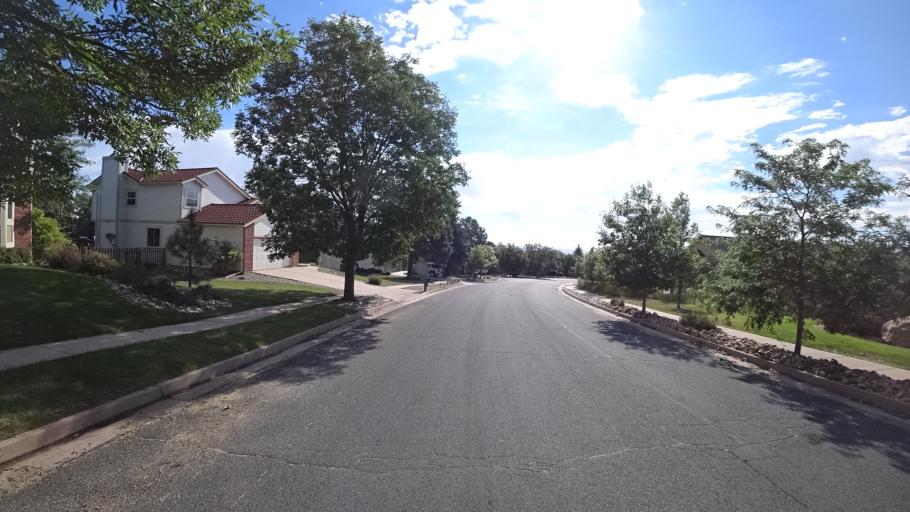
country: US
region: Colorado
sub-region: El Paso County
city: Fort Carson
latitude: 38.7611
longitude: -104.8290
